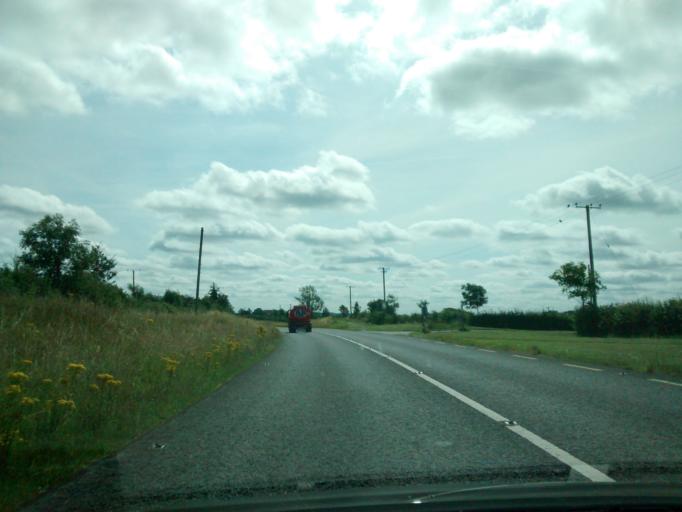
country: IE
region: Leinster
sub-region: An Iarmhi
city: Moate
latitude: 53.3841
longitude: -7.6801
